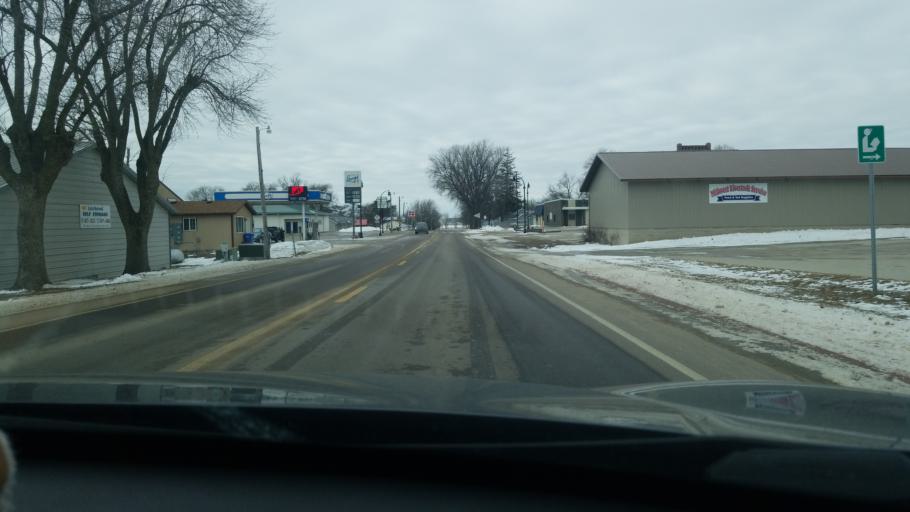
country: US
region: South Dakota
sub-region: Minnehaha County
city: Brandon
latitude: 43.4529
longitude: -96.4330
